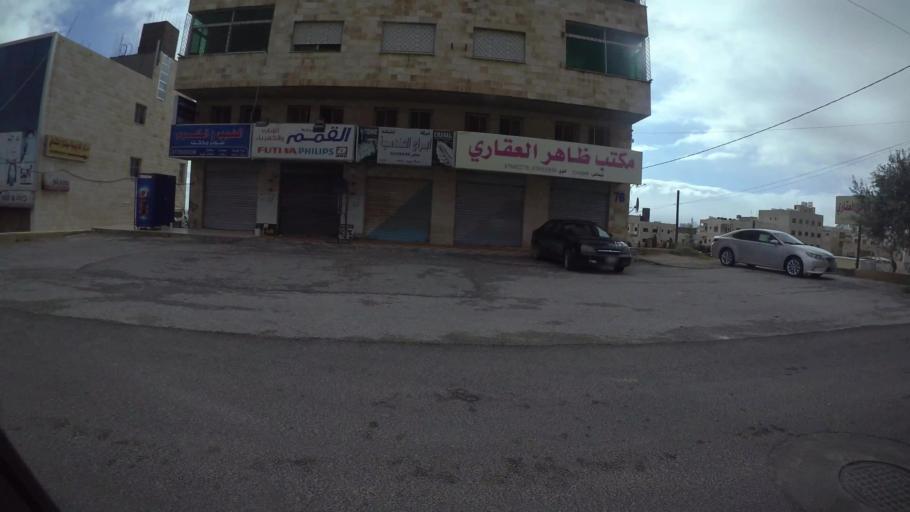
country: JO
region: Amman
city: Al Jubayhah
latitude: 32.0525
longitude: 35.8860
